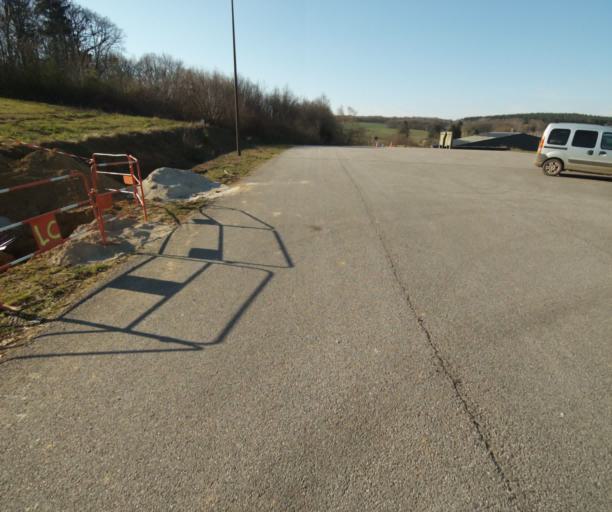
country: FR
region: Limousin
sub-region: Departement de la Correze
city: Chamboulive
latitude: 45.4677
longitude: 1.7254
